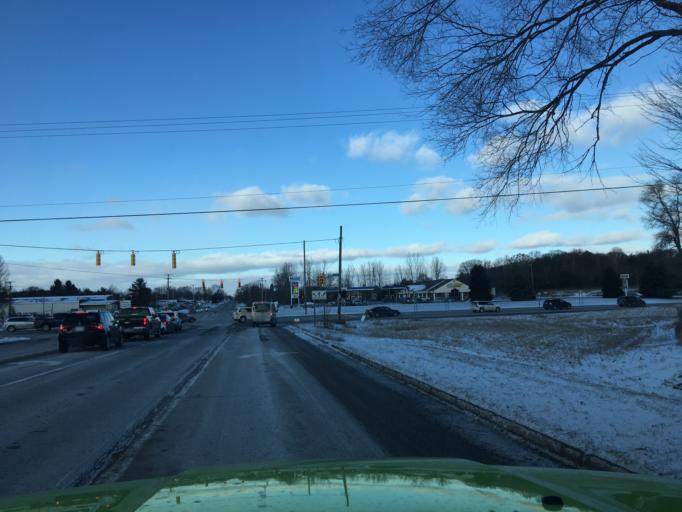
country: US
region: Michigan
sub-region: Kent County
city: Cedar Springs
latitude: 43.1777
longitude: -85.5510
